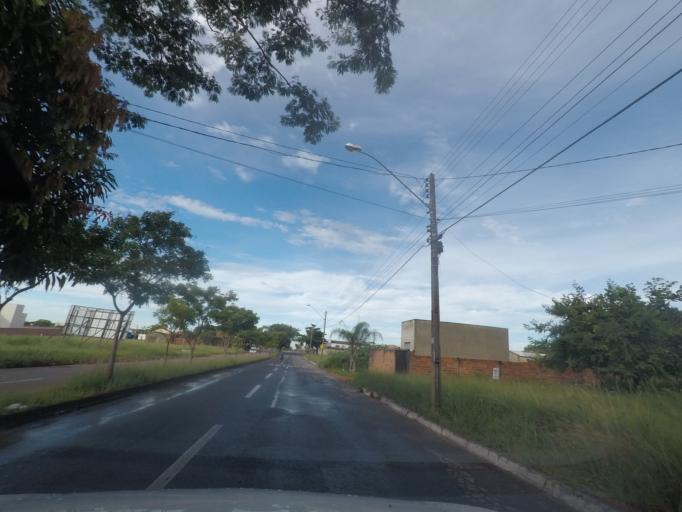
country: BR
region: Goias
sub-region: Aparecida De Goiania
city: Aparecida de Goiania
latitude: -16.7894
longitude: -49.3689
